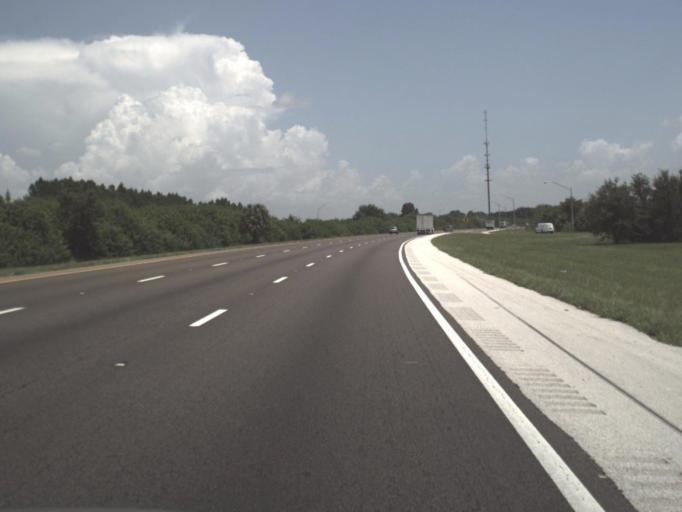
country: US
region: Florida
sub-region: Hillsborough County
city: Ruskin
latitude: 27.6865
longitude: -82.4202
